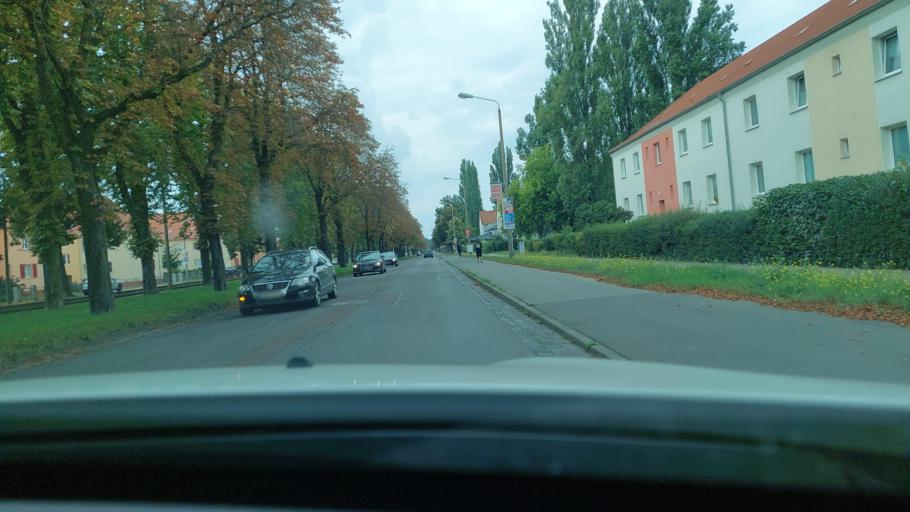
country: DE
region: Brandenburg
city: Brandenburg an der Havel
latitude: 52.4254
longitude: 12.5170
